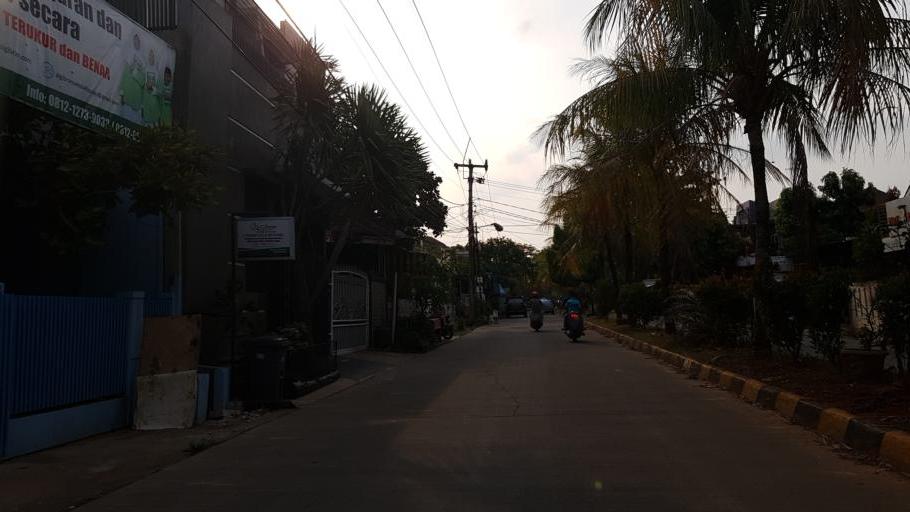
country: ID
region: West Java
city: Sawangan
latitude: -6.3723
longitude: 106.7931
